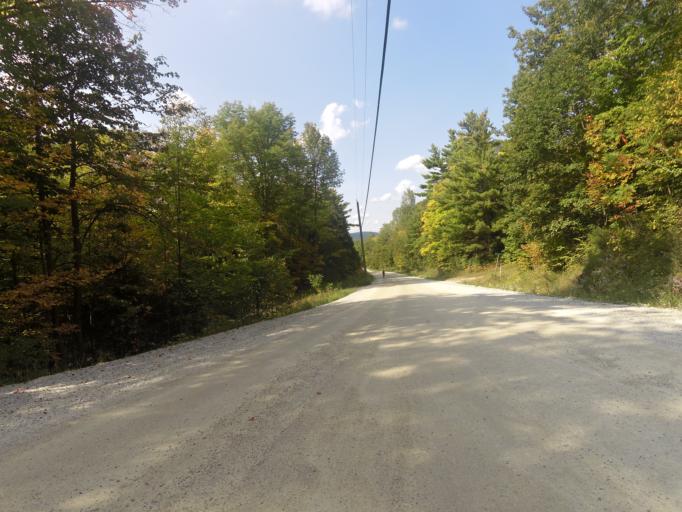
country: CA
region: Ontario
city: Renfrew
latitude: 45.1515
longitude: -76.6793
